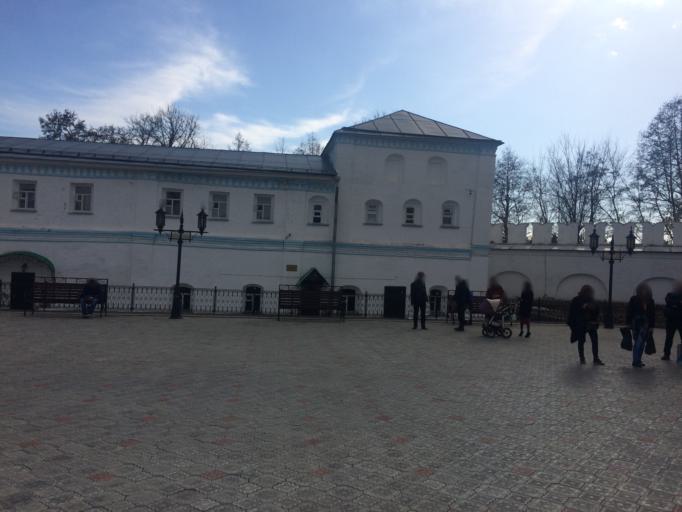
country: RU
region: Tatarstan
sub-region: Zelenodol'skiy Rayon
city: Vasil'yevo
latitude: 55.9020
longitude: 48.7287
